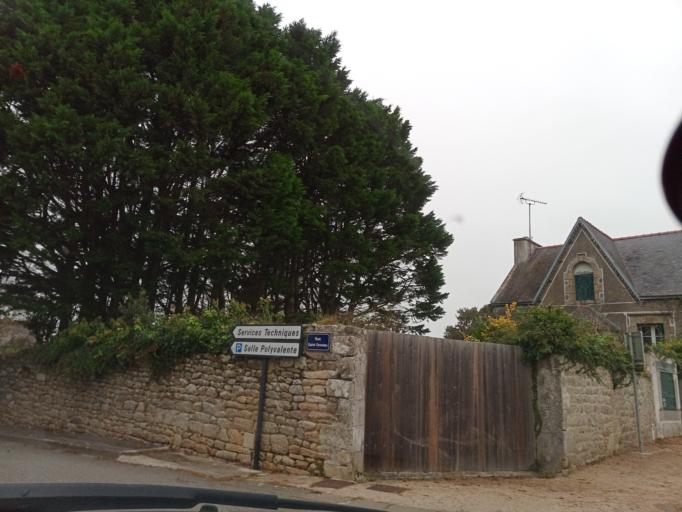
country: FR
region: Brittany
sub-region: Departement du Finistere
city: Esquibien
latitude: 48.0250
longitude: -4.5622
